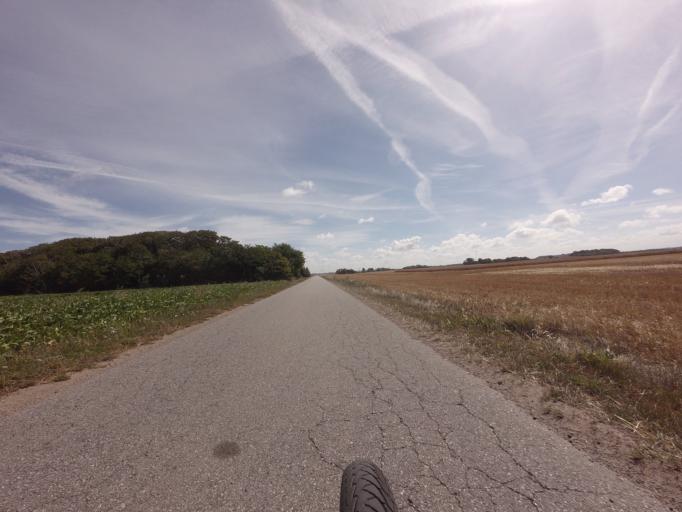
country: DK
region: North Denmark
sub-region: Jammerbugt Kommune
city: Pandrup
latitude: 57.3428
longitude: 9.7859
